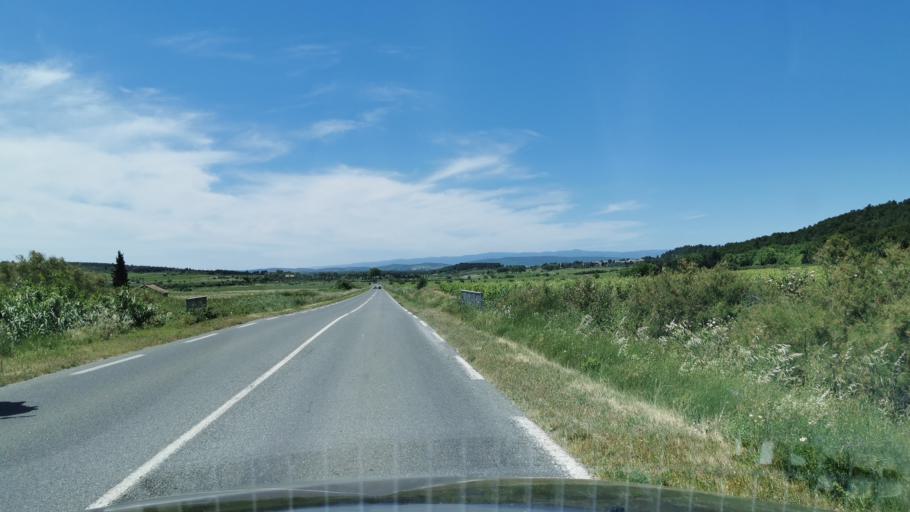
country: FR
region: Languedoc-Roussillon
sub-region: Departement de l'Aude
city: Moussan
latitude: 43.2101
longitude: 2.9459
